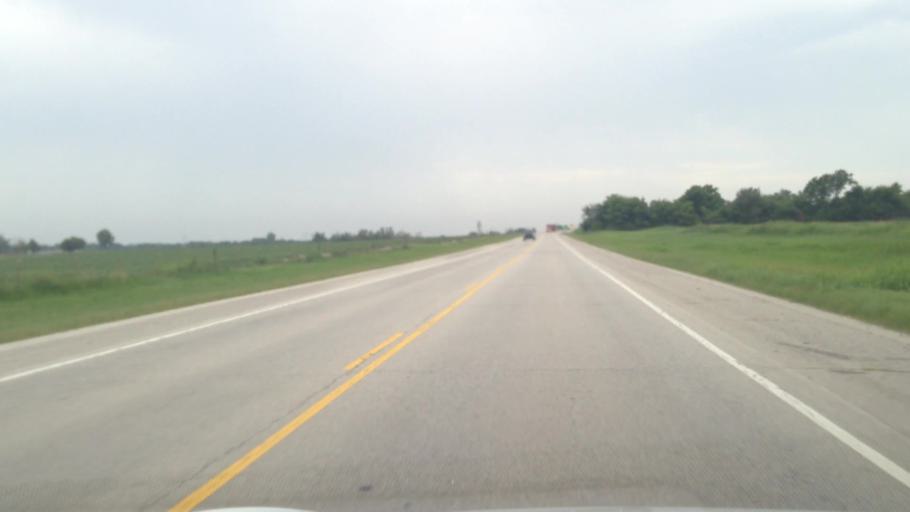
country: US
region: Oklahoma
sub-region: Delaware County
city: Cleora
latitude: 36.6336
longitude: -94.9815
